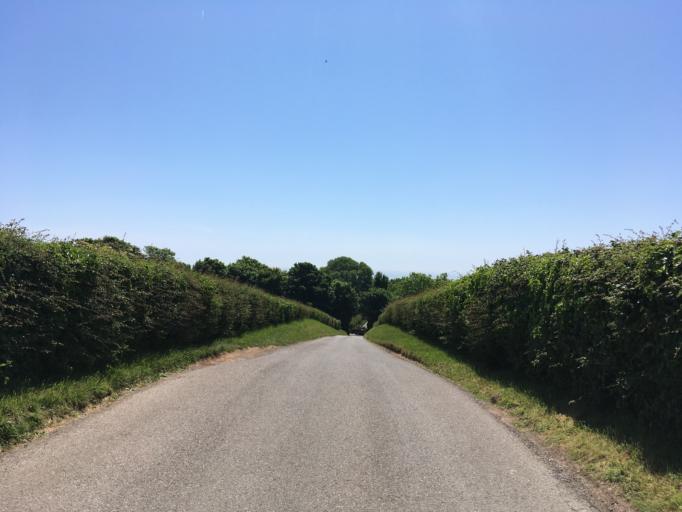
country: GB
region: England
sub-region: Devon
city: Dartmouth
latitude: 50.3505
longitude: -3.5374
